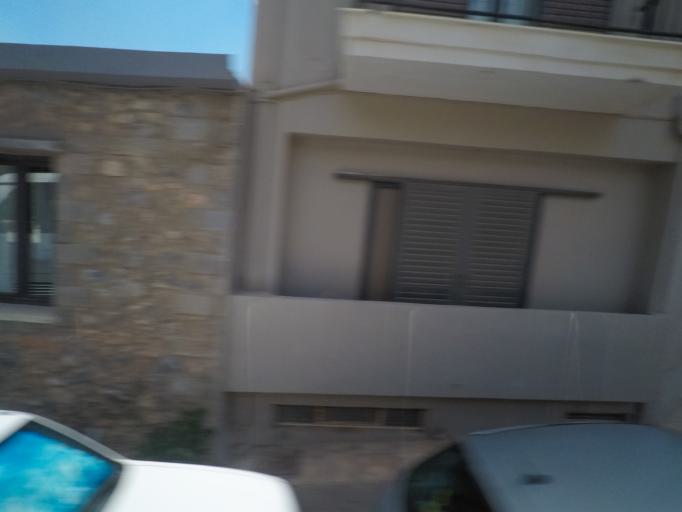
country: GR
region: Crete
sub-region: Nomos Lasithiou
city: Agios Nikolaos
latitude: 35.1935
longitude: 25.7152
